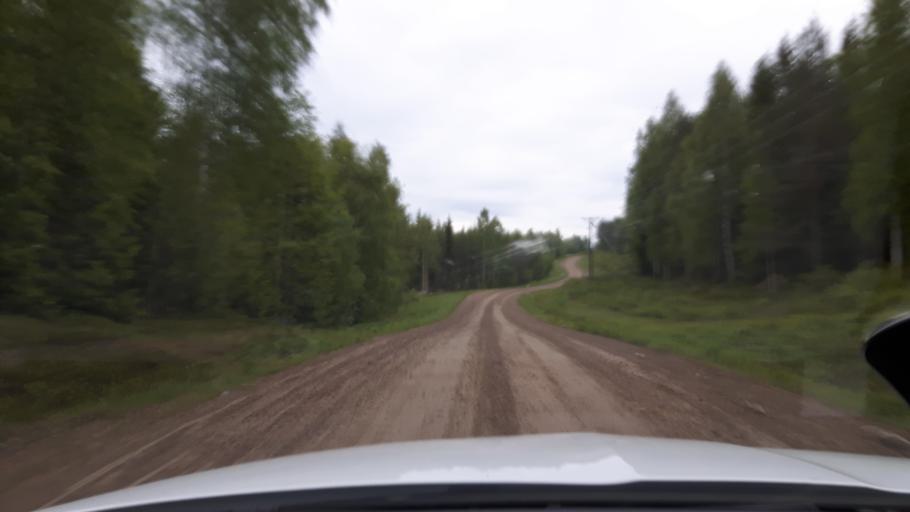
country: SE
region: Vaesternorrland
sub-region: Ange Kommun
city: Ange
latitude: 62.1596
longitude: 15.6610
